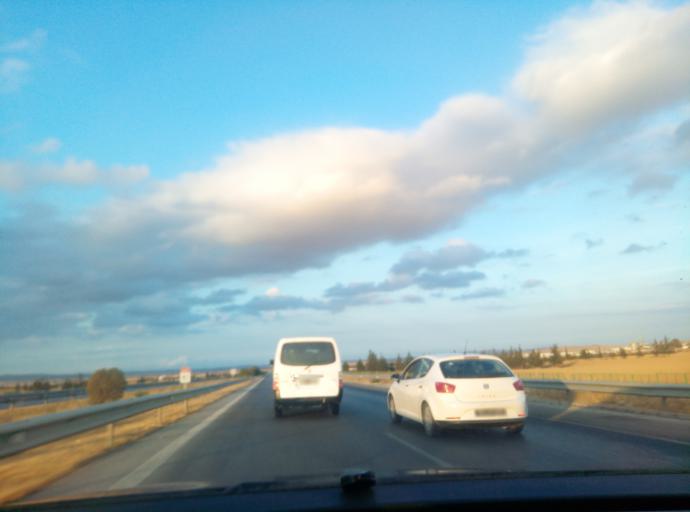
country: TN
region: Manouba
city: El Battan
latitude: 36.6870
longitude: 9.9212
